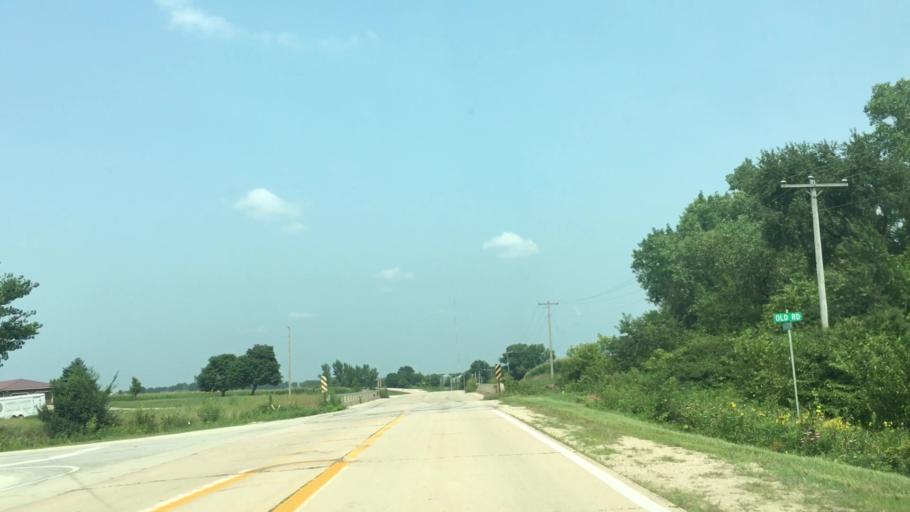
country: US
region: Iowa
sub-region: Fayette County
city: Oelwein
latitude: 42.6613
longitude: -91.8972
